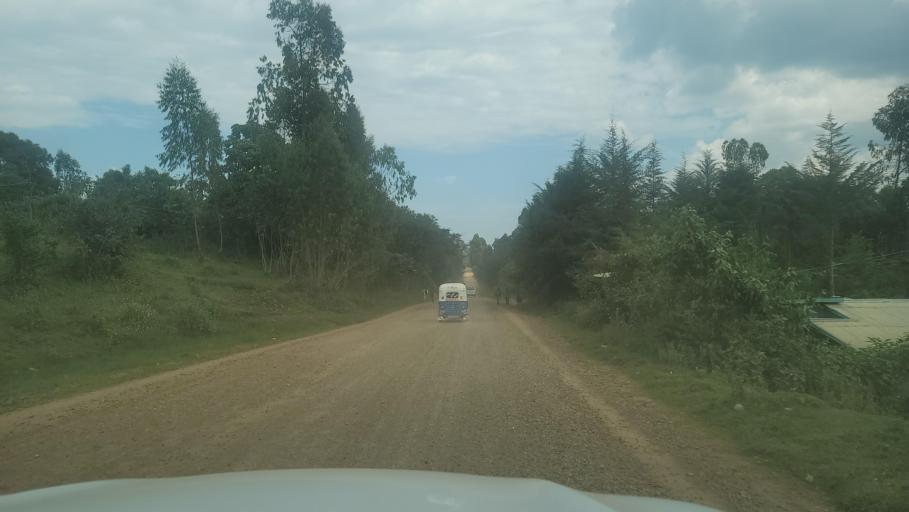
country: ET
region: Oromiya
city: Agaro
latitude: 7.7508
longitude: 36.2621
